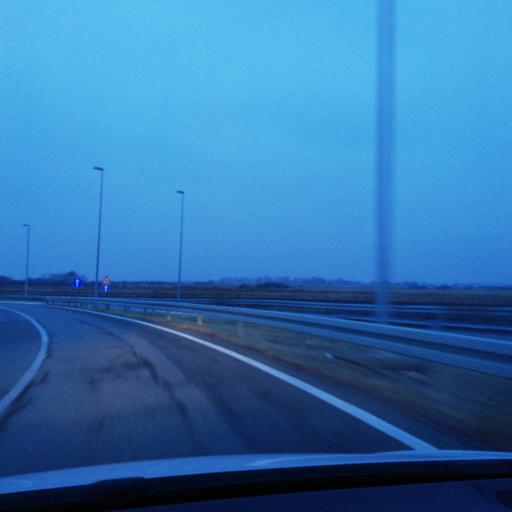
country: RS
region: Autonomna Pokrajina Vojvodina
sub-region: Sremski Okrug
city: Ruma
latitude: 44.9638
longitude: 19.8130
